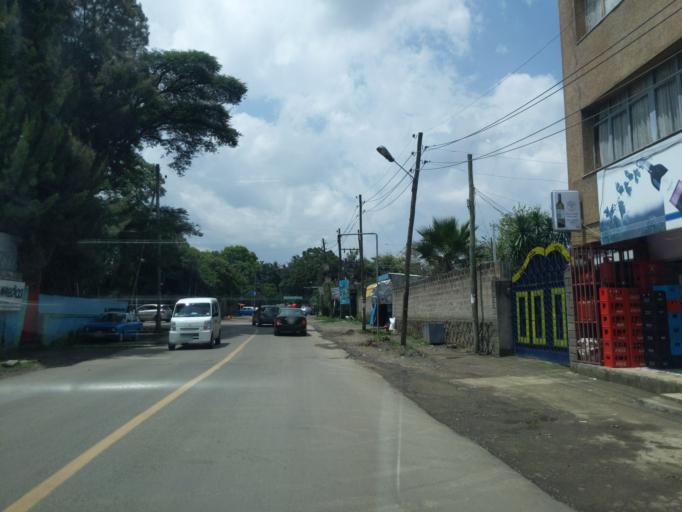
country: ET
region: Adis Abeba
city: Addis Ababa
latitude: 9.0181
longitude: 38.7769
